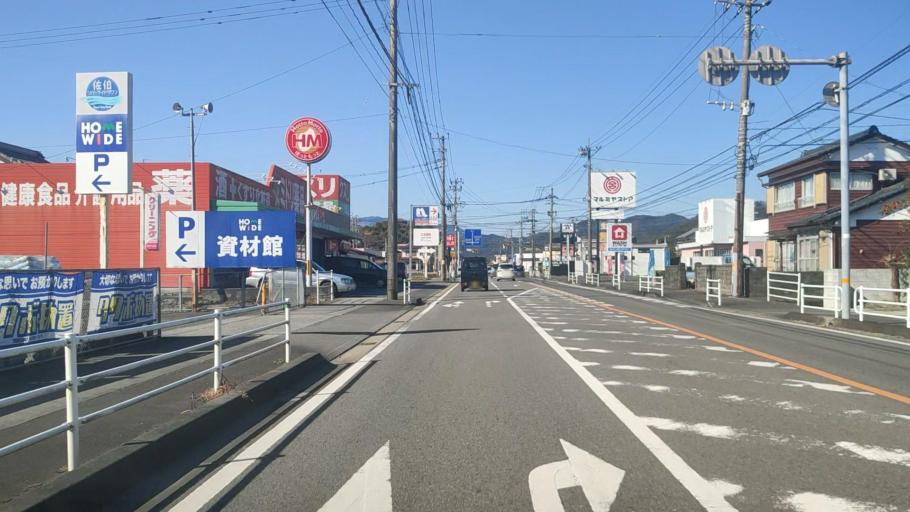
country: JP
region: Oita
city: Saiki
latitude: 32.9454
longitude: 131.9029
